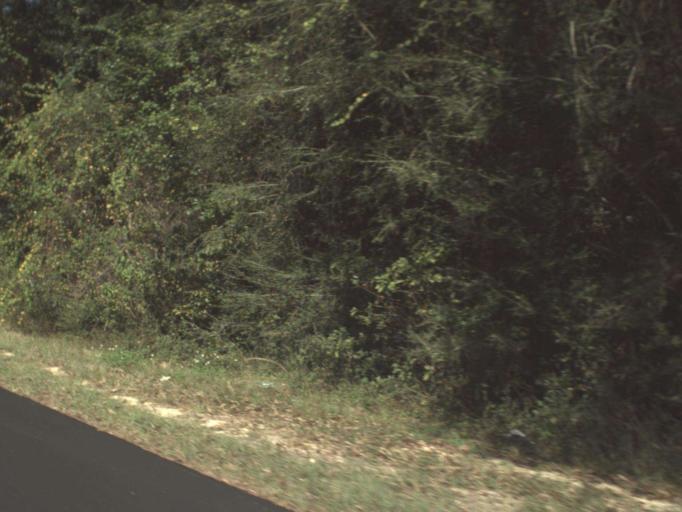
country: US
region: Florida
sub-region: Walton County
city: DeFuniak Springs
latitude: 30.7823
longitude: -86.1706
